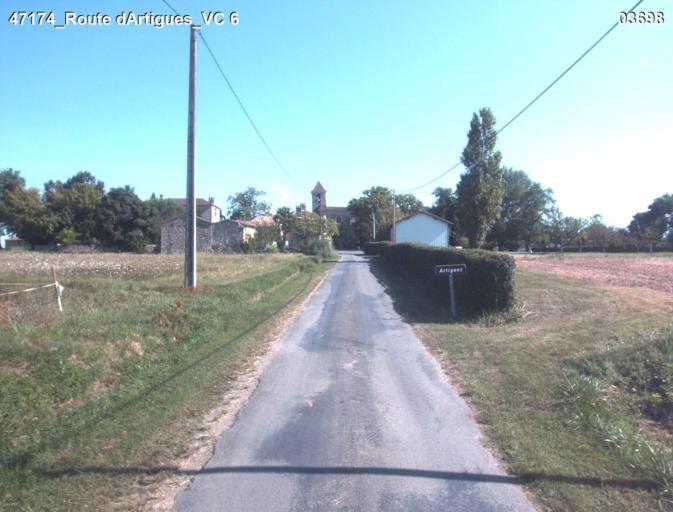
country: FR
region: Aquitaine
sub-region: Departement du Lot-et-Garonne
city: Mezin
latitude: 44.0393
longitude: 0.3379
